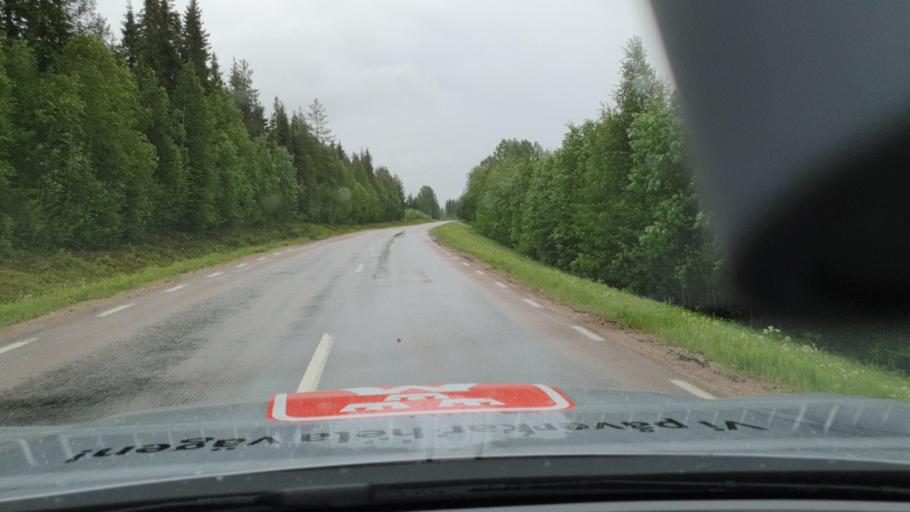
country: SE
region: Norrbotten
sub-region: Overtornea Kommun
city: OEvertornea
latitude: 66.4343
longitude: 23.3350
